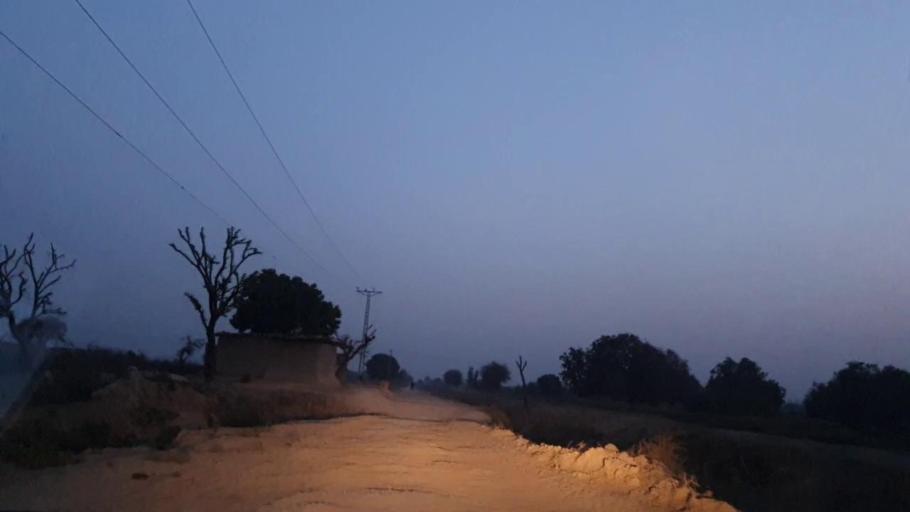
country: PK
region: Sindh
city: Tando Ghulam Ali
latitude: 25.1009
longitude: 68.9117
